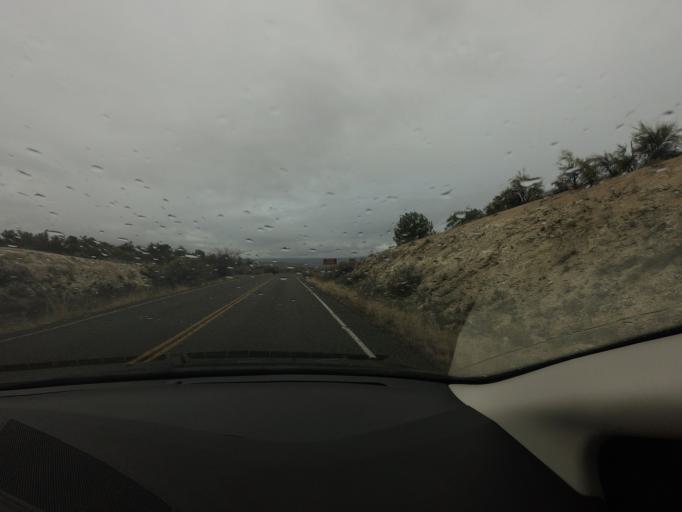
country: US
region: Arizona
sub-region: Yavapai County
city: Camp Verde
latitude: 34.6158
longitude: -111.8439
